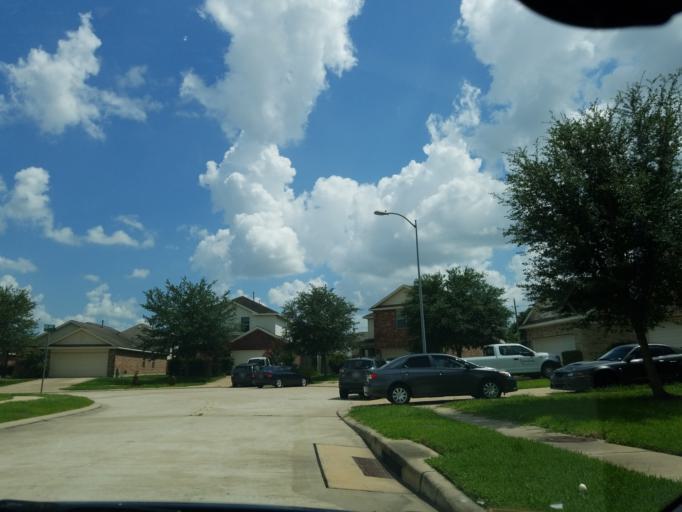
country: US
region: Texas
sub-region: Harris County
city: Cypress
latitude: 29.8776
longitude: -95.7286
